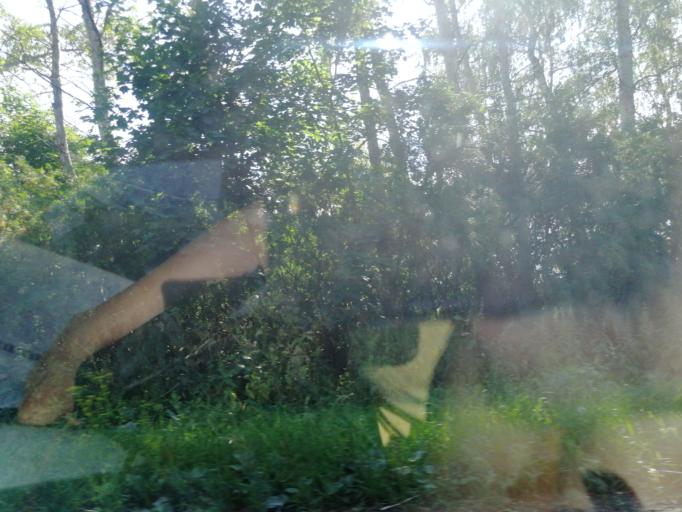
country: RU
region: Tula
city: Tovarkovskiy
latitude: 53.6157
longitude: 38.2698
